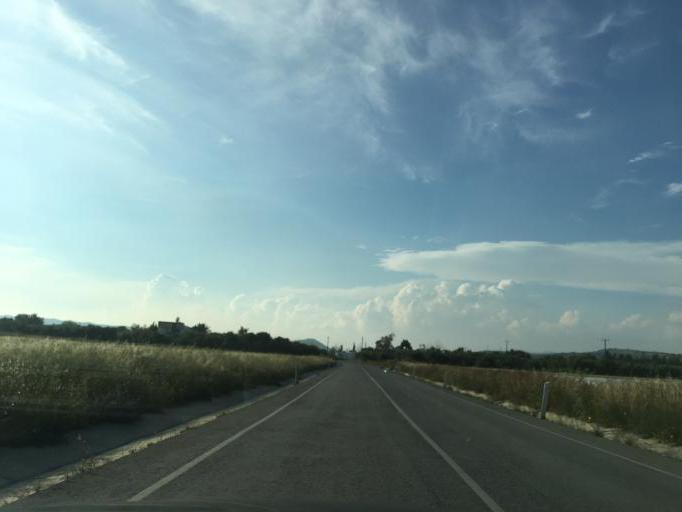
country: CY
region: Larnaka
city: Kofinou
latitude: 34.7476
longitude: 33.3189
